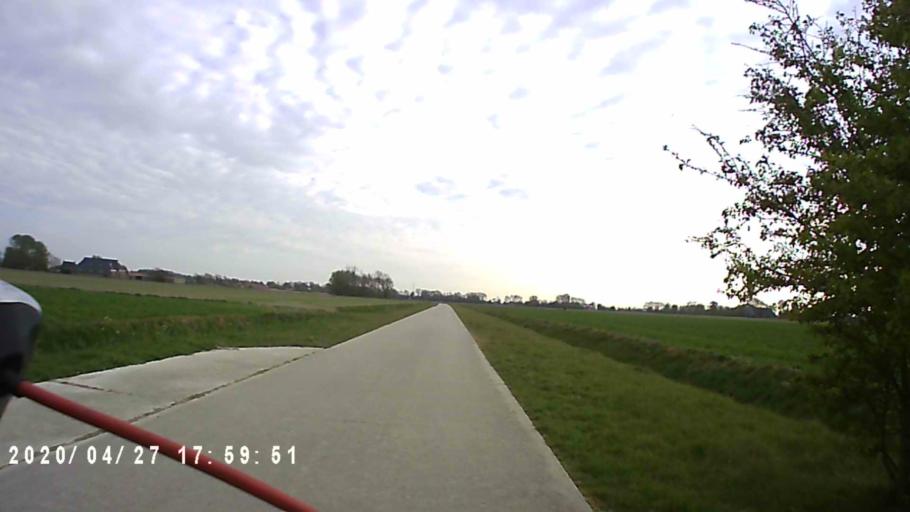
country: NL
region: Groningen
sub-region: Gemeente Winsum
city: Winsum
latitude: 53.4099
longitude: 6.4542
